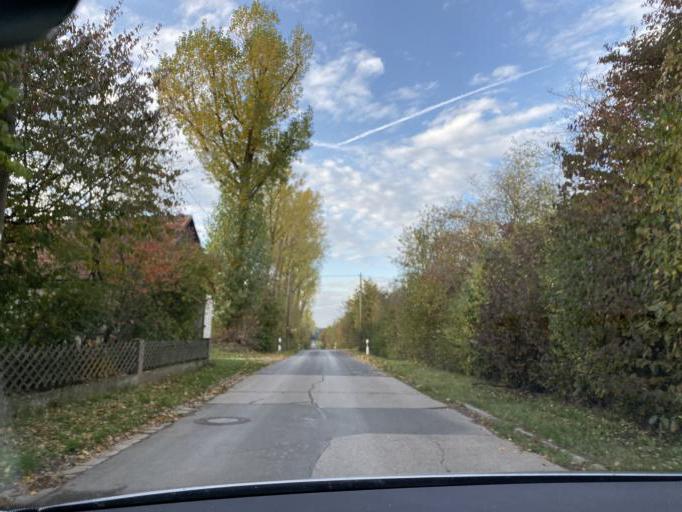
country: DE
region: Bavaria
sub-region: Regierungsbezirk Mittelfranken
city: Puschendorf
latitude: 49.5439
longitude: 10.8274
